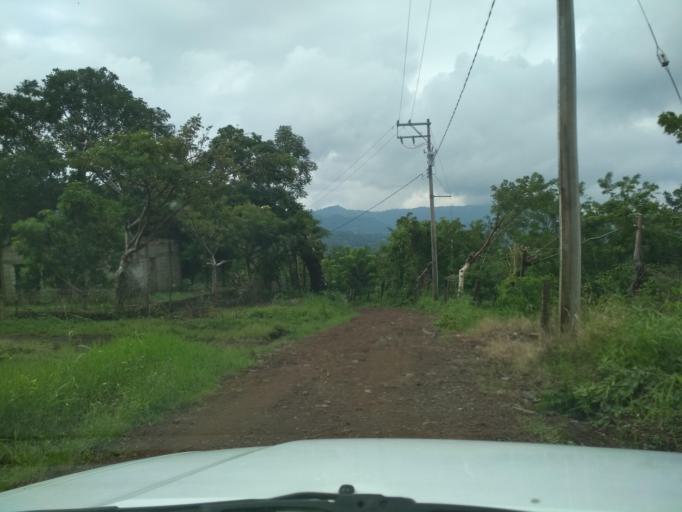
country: MX
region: Veracruz
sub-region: San Andres Tuxtla
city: Matacapan
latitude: 18.4362
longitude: -95.1503
